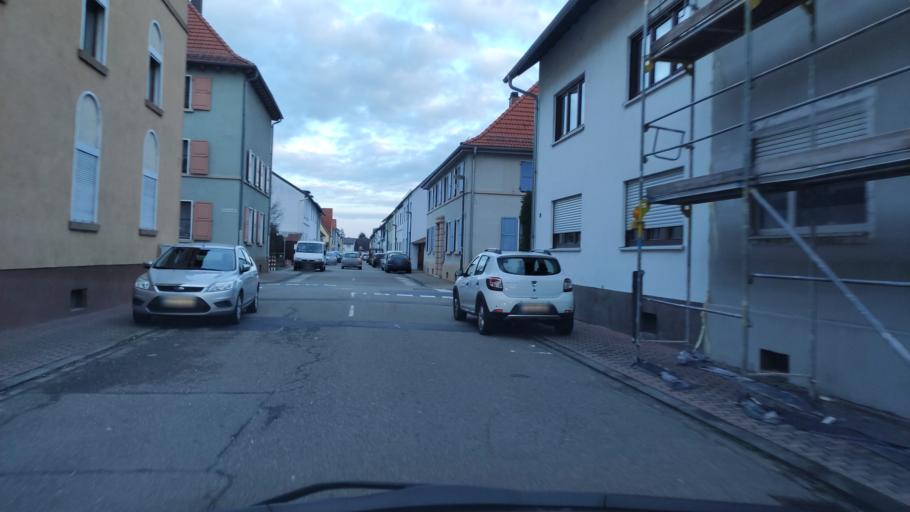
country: DE
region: Baden-Wuerttemberg
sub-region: Karlsruhe Region
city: Hockenheim
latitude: 49.3198
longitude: 8.5565
